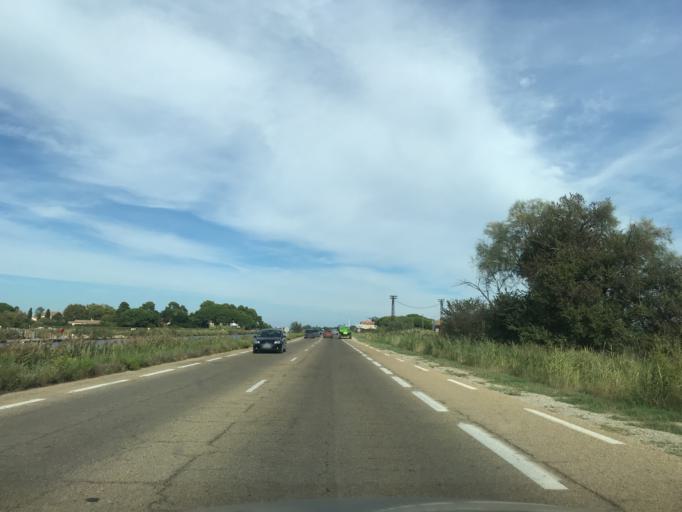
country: FR
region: Languedoc-Roussillon
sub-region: Departement du Gard
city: Le Grau-du-Roi
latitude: 43.5491
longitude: 4.1641
